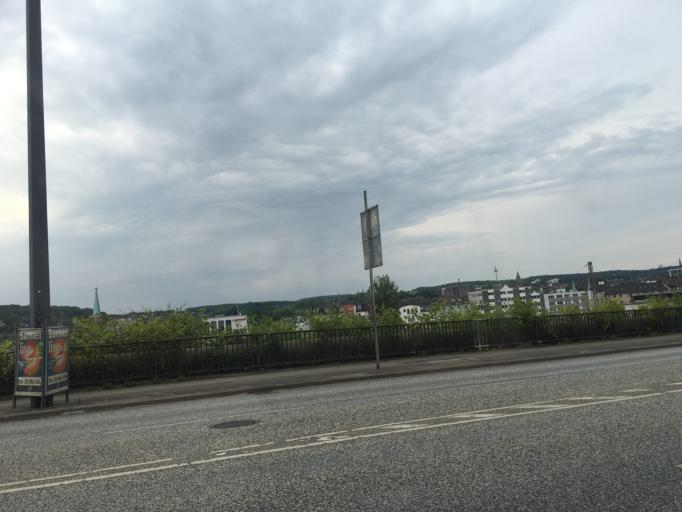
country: DE
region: North Rhine-Westphalia
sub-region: Regierungsbezirk Dusseldorf
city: Wuppertal
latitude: 51.2486
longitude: 7.1396
